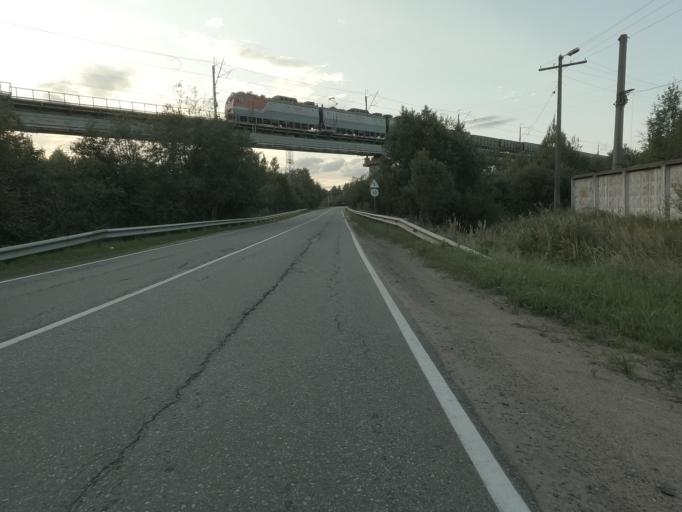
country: RU
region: Leningrad
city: Mga
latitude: 59.7580
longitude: 31.0190
